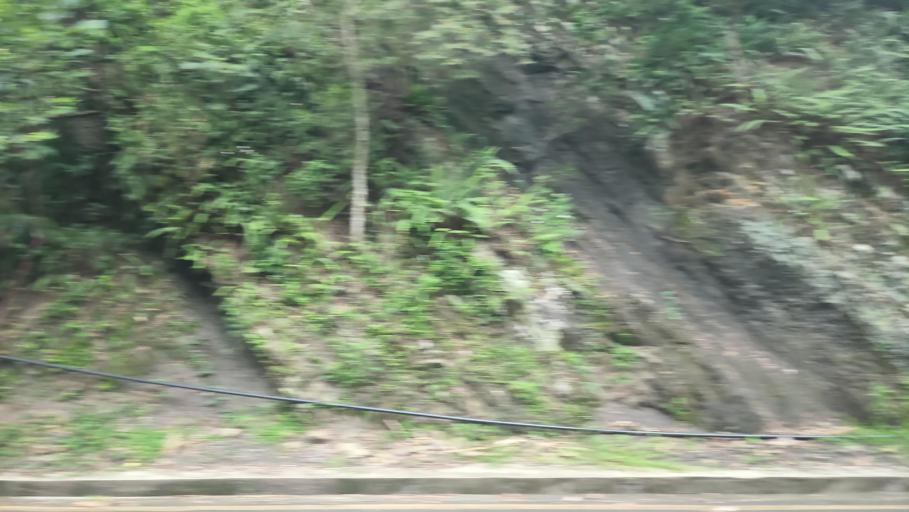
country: TW
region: Taiwan
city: Daxi
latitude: 24.8473
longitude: 121.4484
